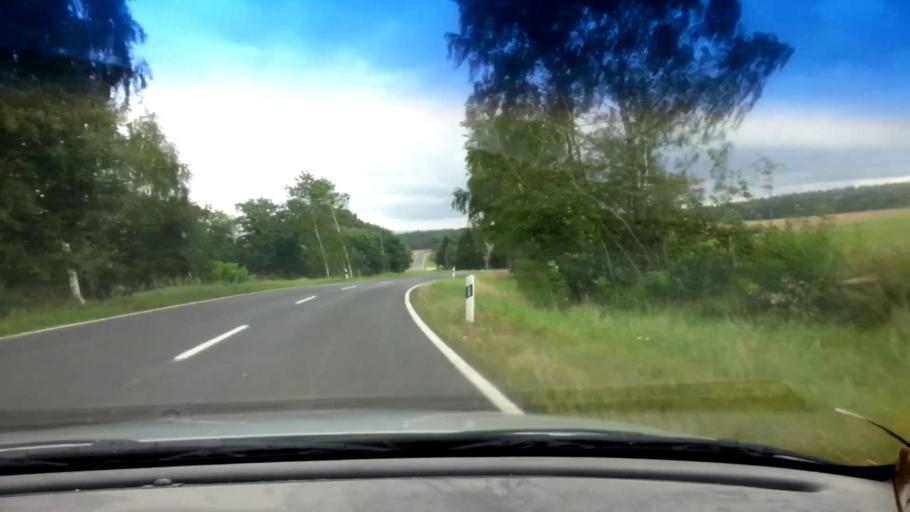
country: DE
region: Bavaria
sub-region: Upper Palatinate
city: Waldsassen
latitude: 50.0346
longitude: 12.2977
